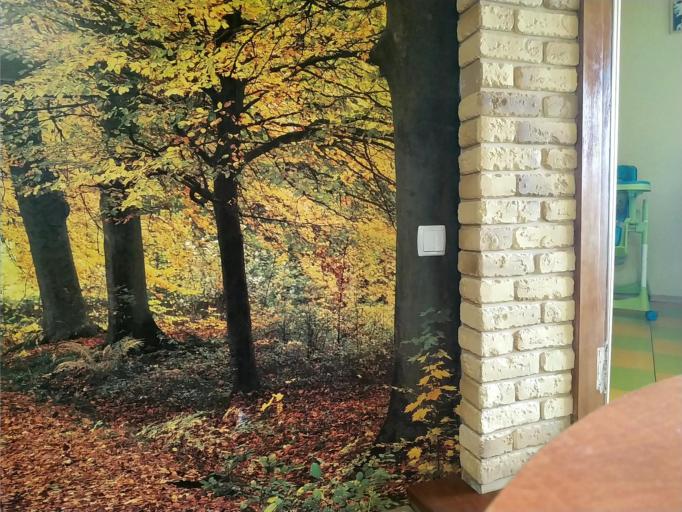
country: RU
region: Smolensk
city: Ozernyy
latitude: 55.4726
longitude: 32.6611
